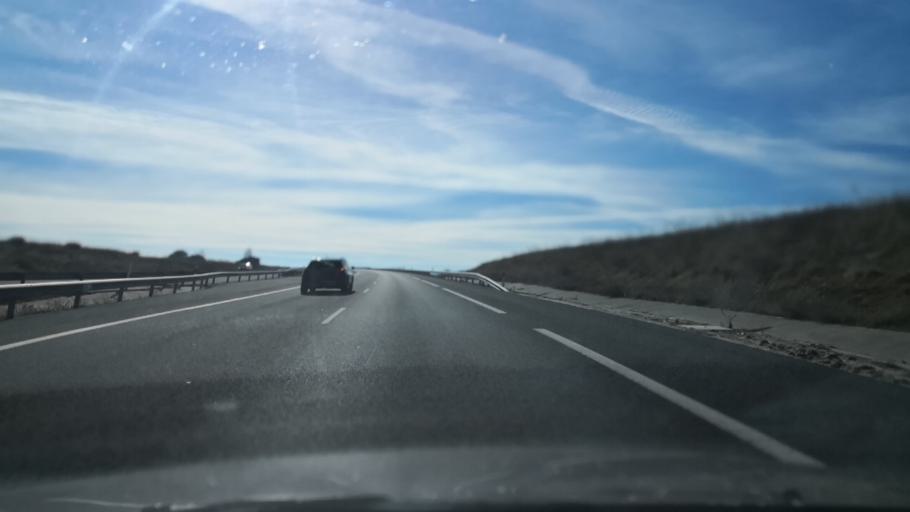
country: ES
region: Castille and Leon
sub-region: Provincia de Avila
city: Crespos
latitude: 40.8636
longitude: -4.9859
